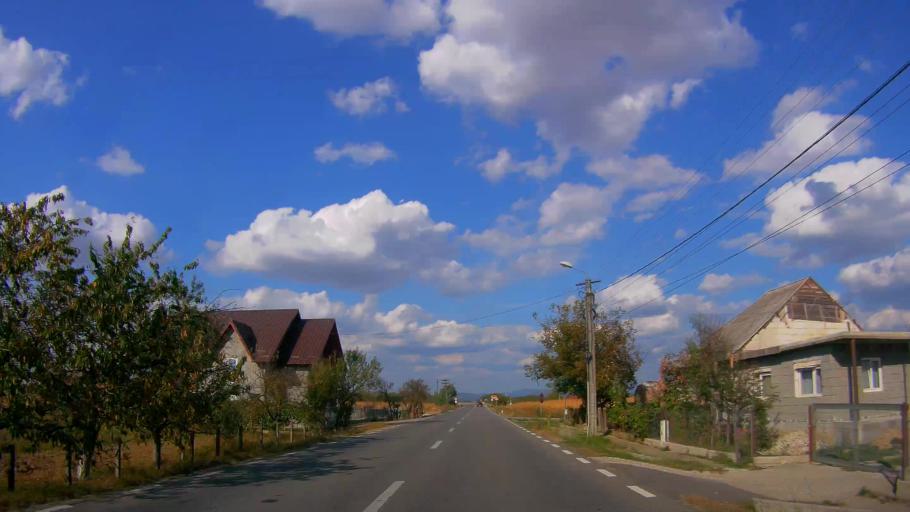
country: RO
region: Satu Mare
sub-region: Comuna Turulung
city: Draguseni
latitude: 47.9123
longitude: 23.0786
